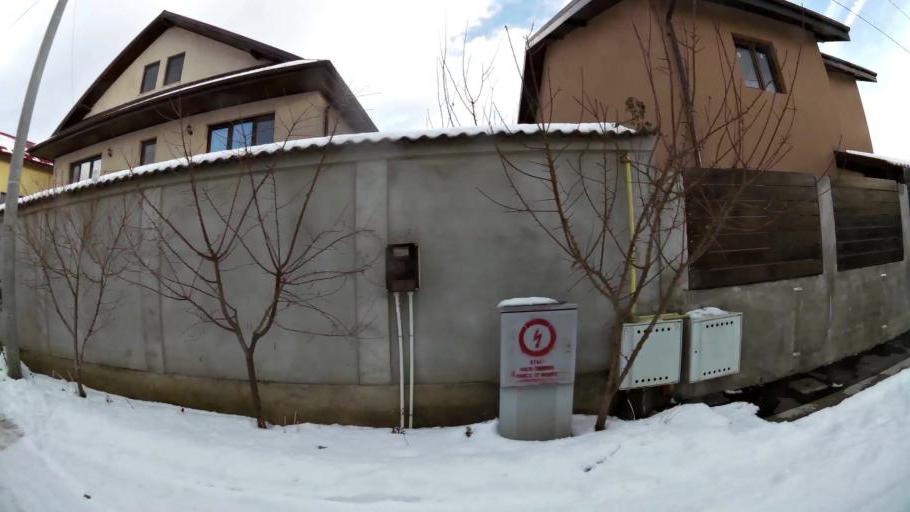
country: RO
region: Ilfov
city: Dobroesti
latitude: 44.4605
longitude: 26.1813
